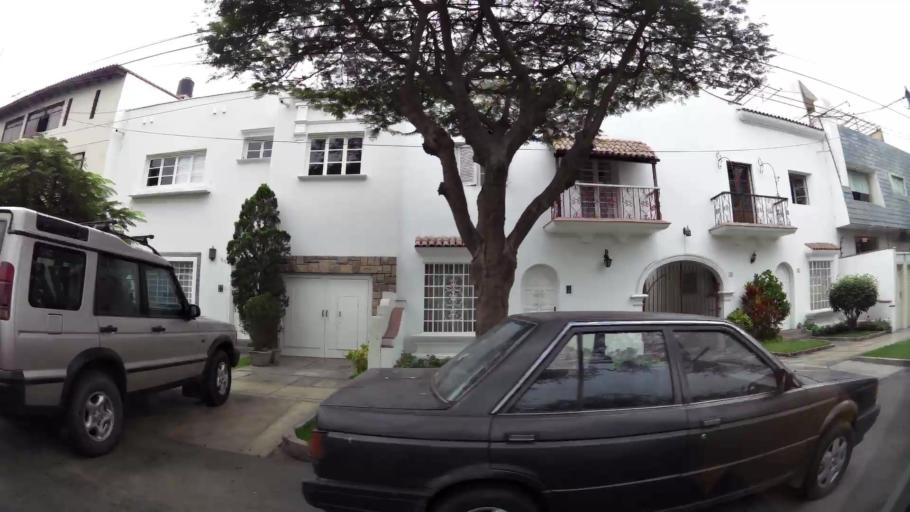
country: PE
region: Lima
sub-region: Lima
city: Surco
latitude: -12.1237
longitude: -77.0190
